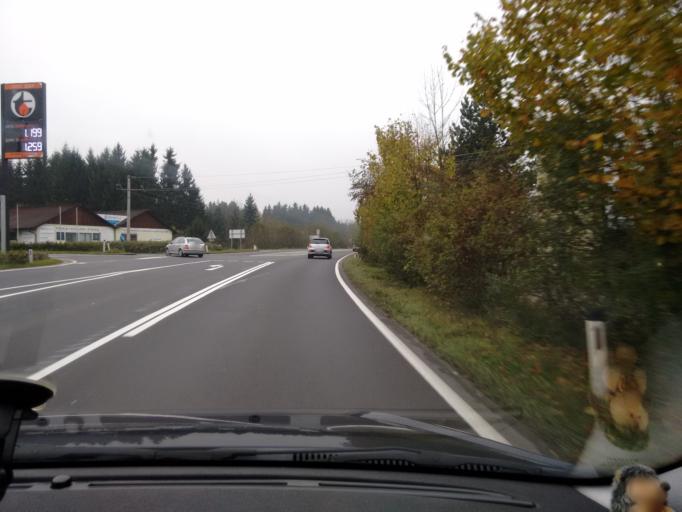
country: AT
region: Upper Austria
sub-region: Wels-Land
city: Sattledt
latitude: 48.0758
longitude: 14.0470
